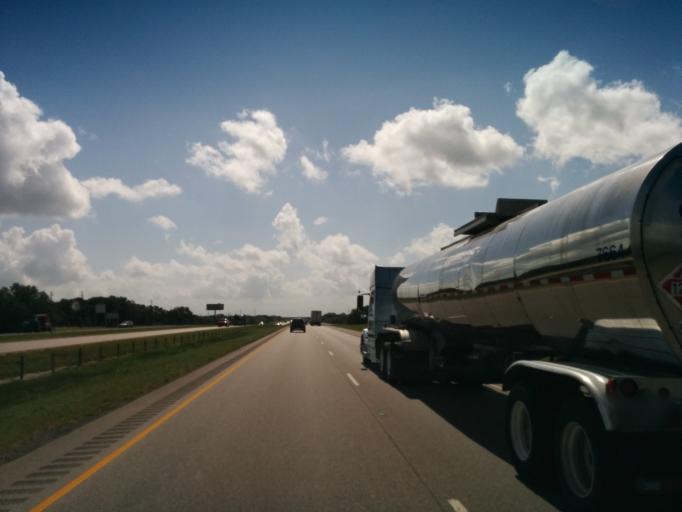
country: US
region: Texas
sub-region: Colorado County
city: Columbus
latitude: 29.6935
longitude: -96.5852
